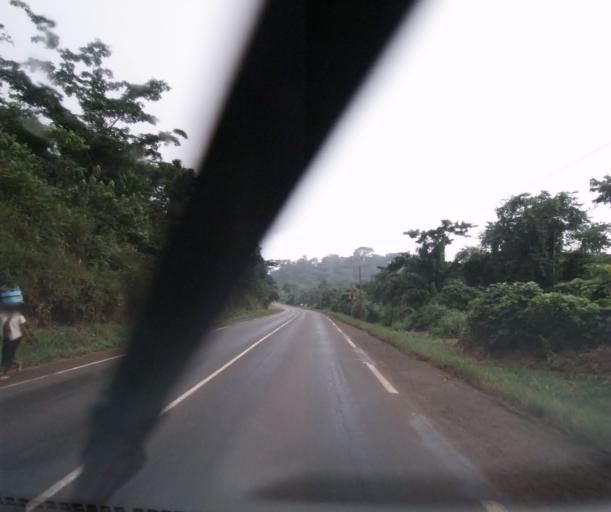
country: CM
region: Centre
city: Mbankomo
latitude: 3.7656
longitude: 11.2023
